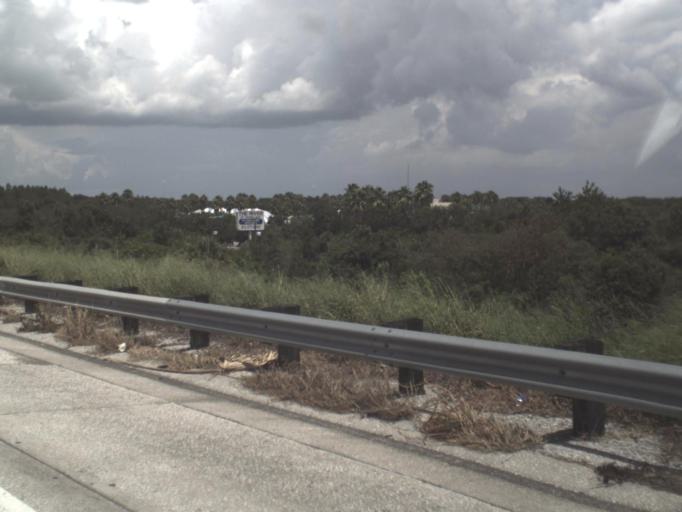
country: US
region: Florida
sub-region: Hillsborough County
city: Mango
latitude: 27.9751
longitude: -82.3261
